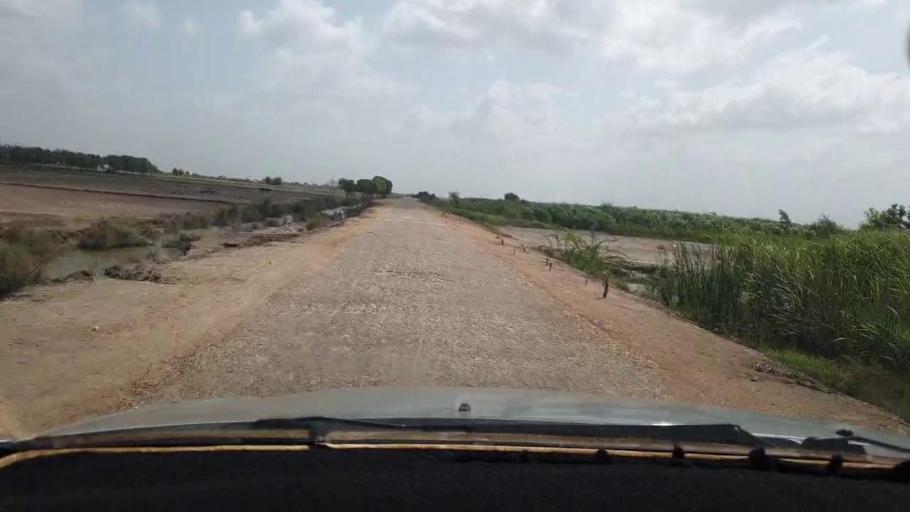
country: PK
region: Sindh
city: Tando Bago
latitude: 24.7207
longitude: 69.1776
